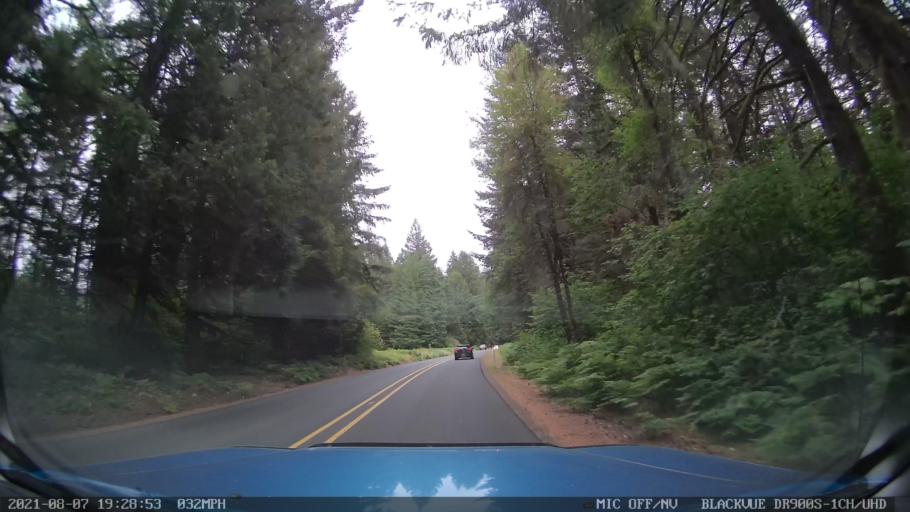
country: US
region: Oregon
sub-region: Linn County
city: Lyons
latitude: 44.8842
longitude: -122.6357
